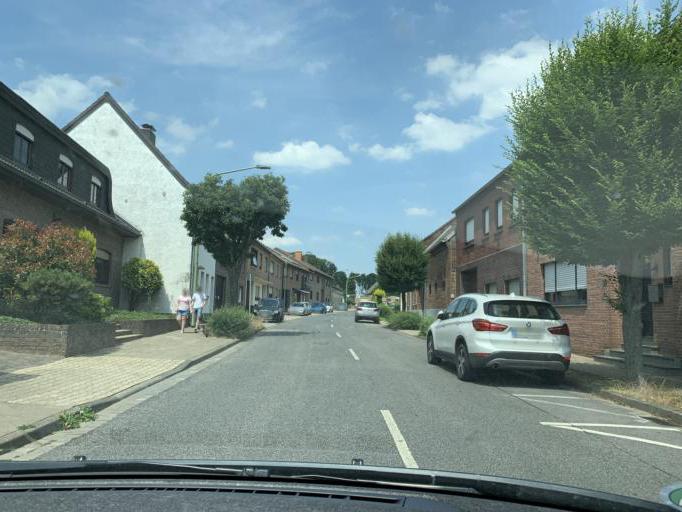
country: DE
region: North Rhine-Westphalia
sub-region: Regierungsbezirk Koln
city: Titz
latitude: 50.9666
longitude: 6.4598
